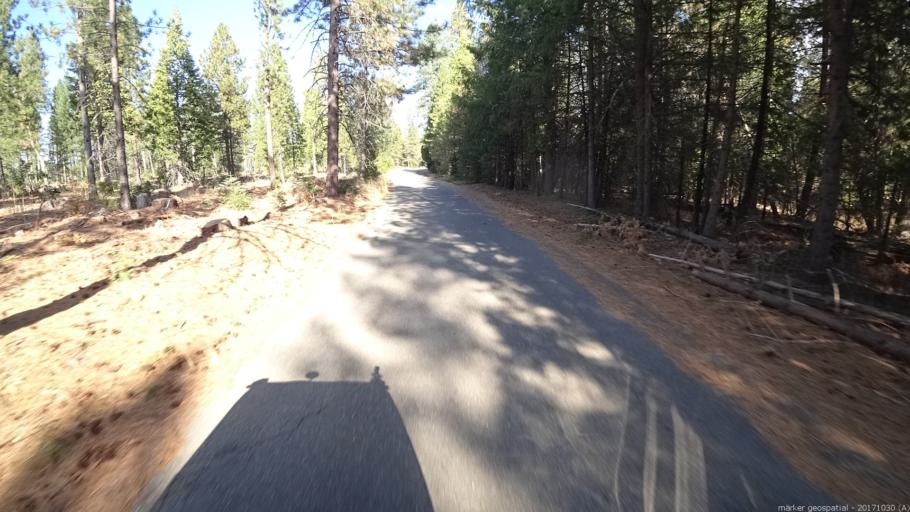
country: US
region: California
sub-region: Shasta County
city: Shingletown
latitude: 40.5098
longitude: -121.7345
